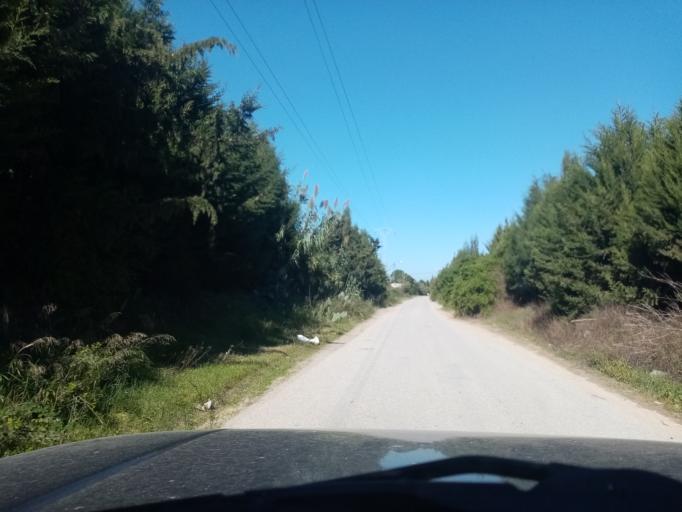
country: TN
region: Nabul
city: Bu `Urqub
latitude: 36.5705
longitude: 10.5763
